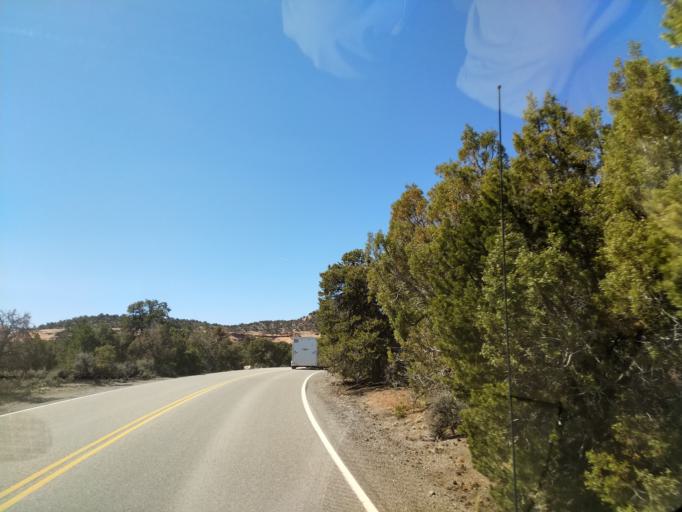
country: US
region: Colorado
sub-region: Mesa County
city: Redlands
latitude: 39.0247
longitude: -108.6587
